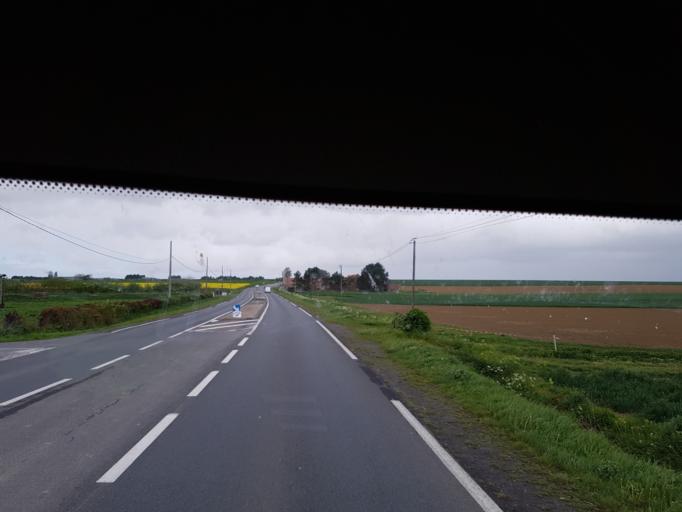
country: FR
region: Nord-Pas-de-Calais
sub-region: Departement du Nord
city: Raillencourt-Sainte-Olle
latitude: 50.2128
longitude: 3.1856
